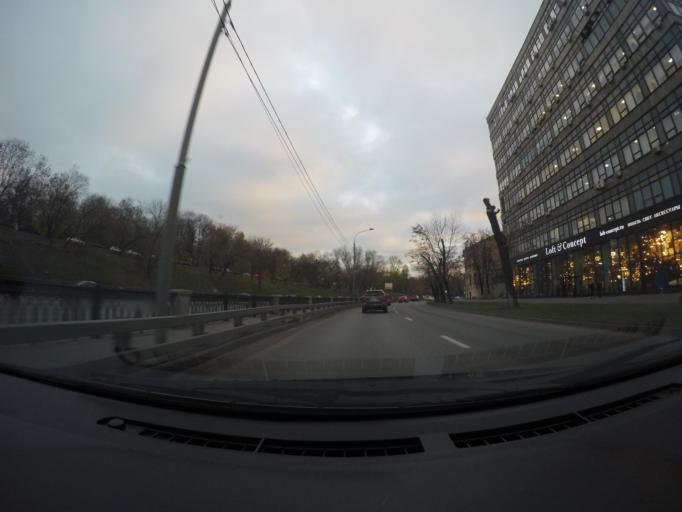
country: RU
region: Moscow
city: Taganskiy
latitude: 55.7537
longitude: 37.6727
